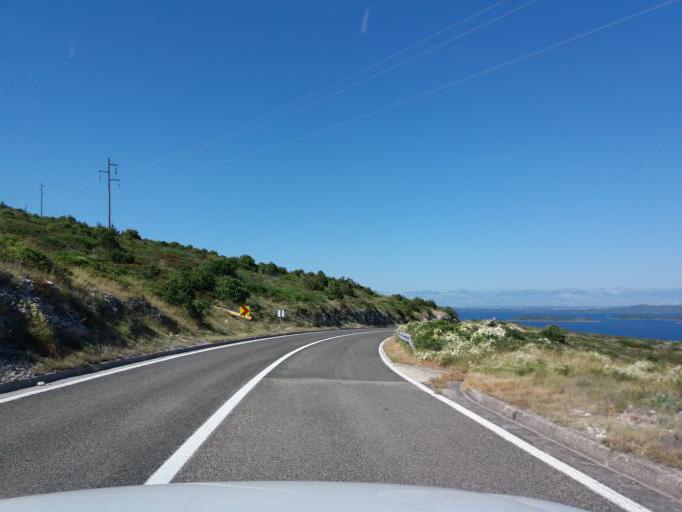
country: HR
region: Zadarska
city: Ugljan
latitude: 44.0454
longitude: 15.0152
